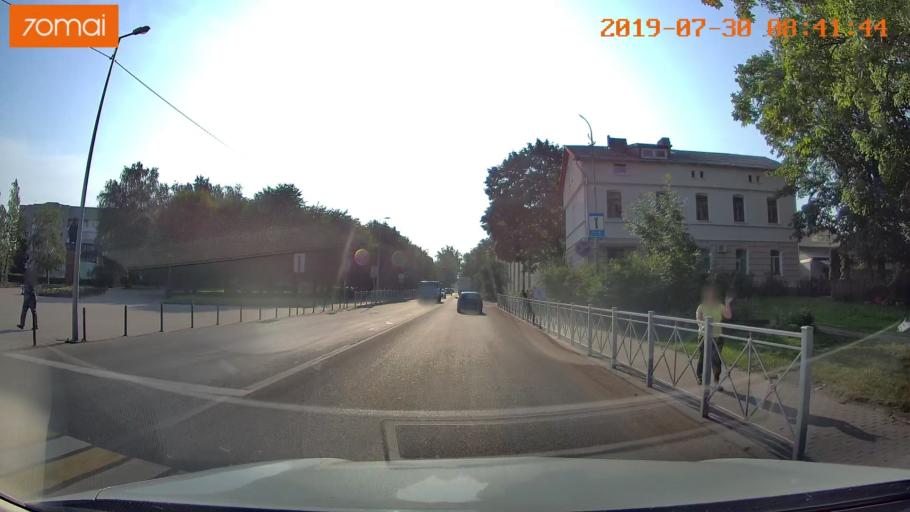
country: RU
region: Kaliningrad
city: Chernyakhovsk
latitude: 54.6301
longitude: 21.8198
